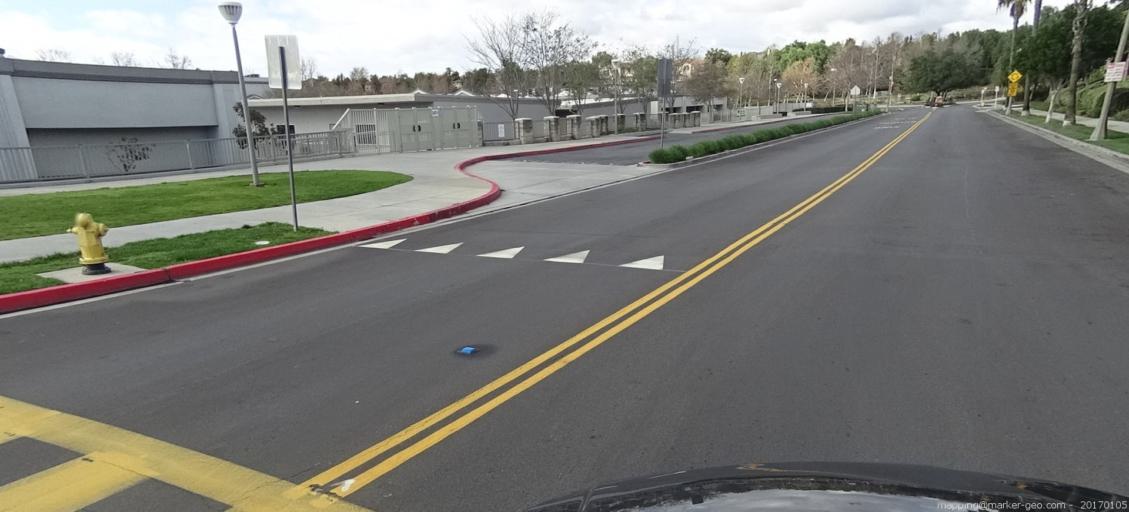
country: US
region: California
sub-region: Orange County
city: Ladera Ranch
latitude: 33.5541
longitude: -117.6354
